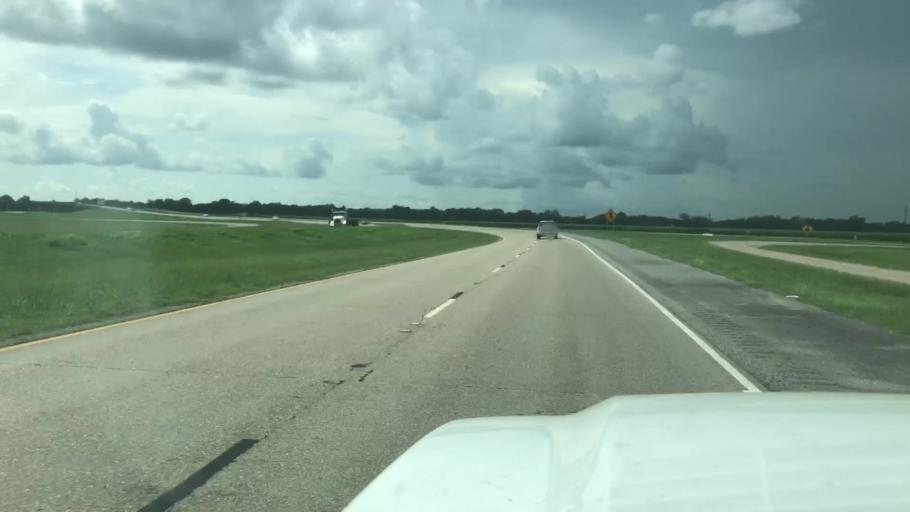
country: US
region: Louisiana
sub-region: Saint Mary Parish
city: Franklin
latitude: 29.7571
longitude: -91.4560
